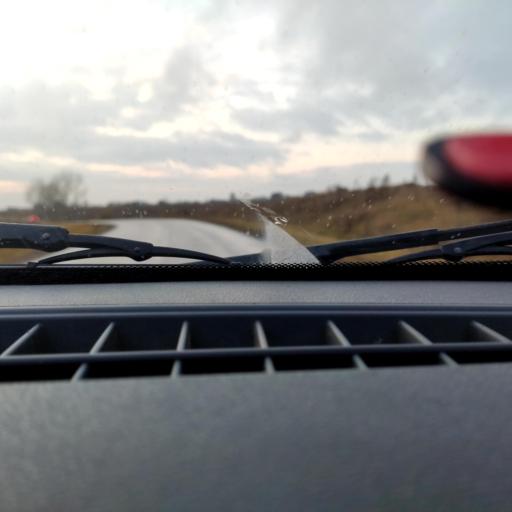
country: RU
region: Bashkortostan
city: Avdon
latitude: 54.5118
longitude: 55.8480
